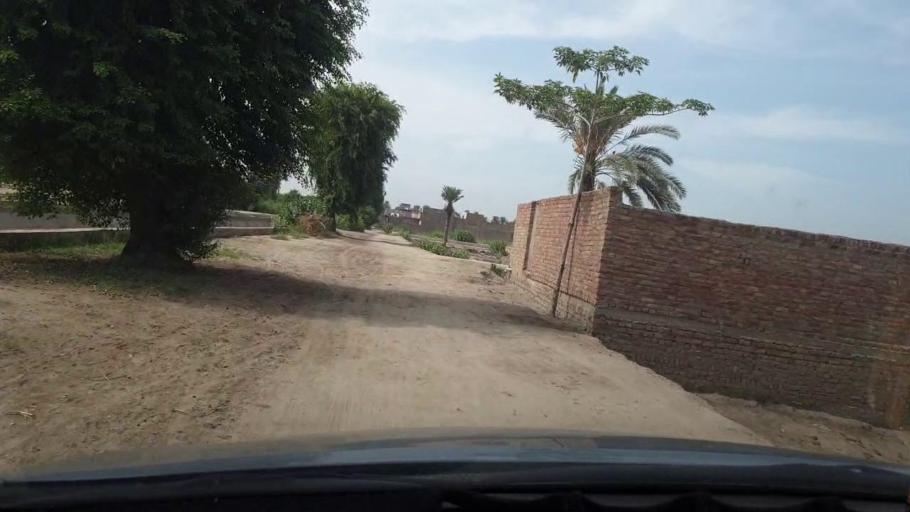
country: PK
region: Sindh
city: Khairpur
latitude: 27.5101
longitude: 68.7599
